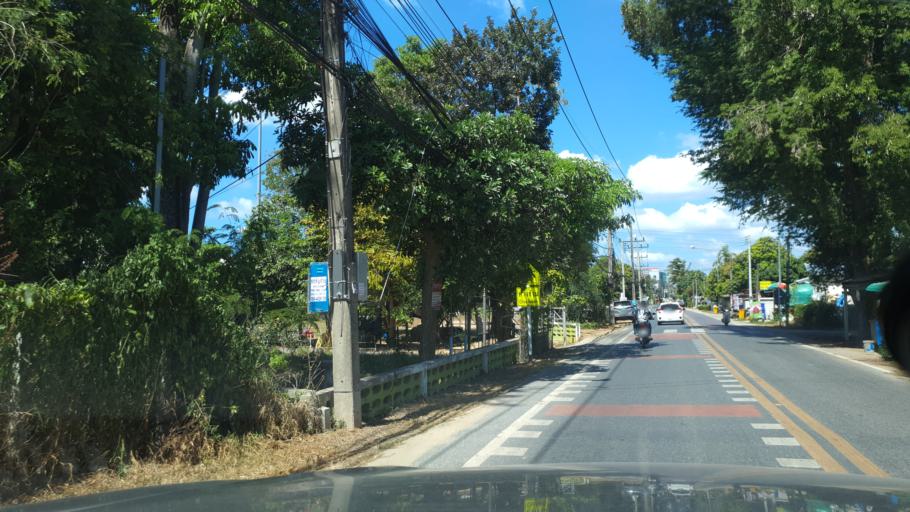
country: TH
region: Phuket
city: Thalang
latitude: 8.1311
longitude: 98.3077
